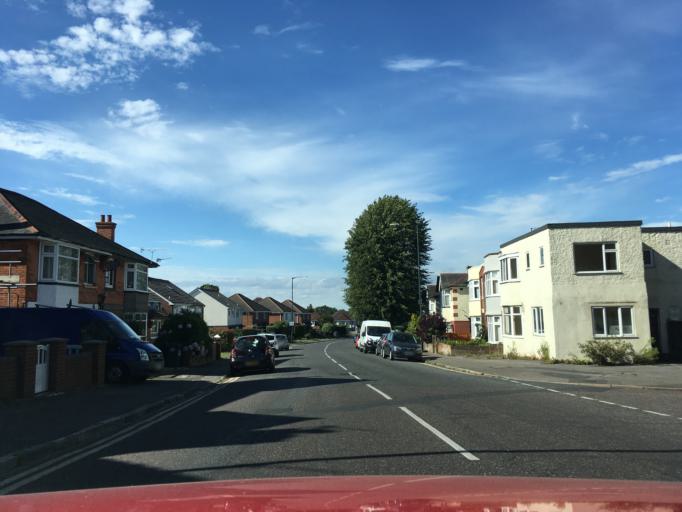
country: GB
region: England
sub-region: Bournemouth
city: Bournemouth
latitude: 50.7588
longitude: -1.8721
